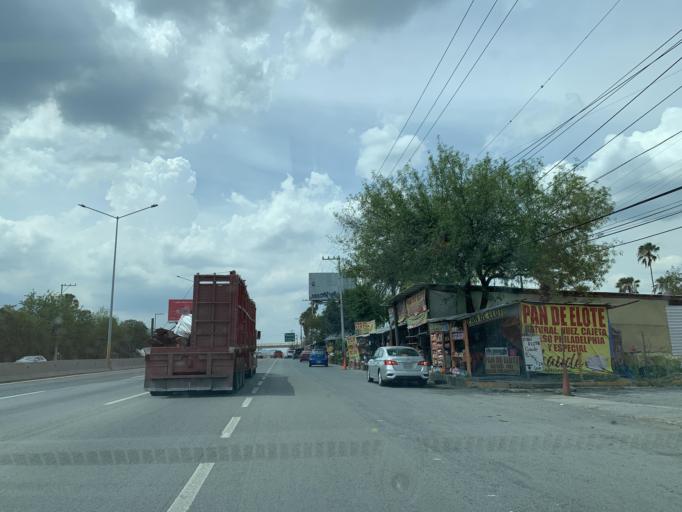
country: MX
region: Nuevo Leon
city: Santiago
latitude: 25.4461
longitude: -100.1582
